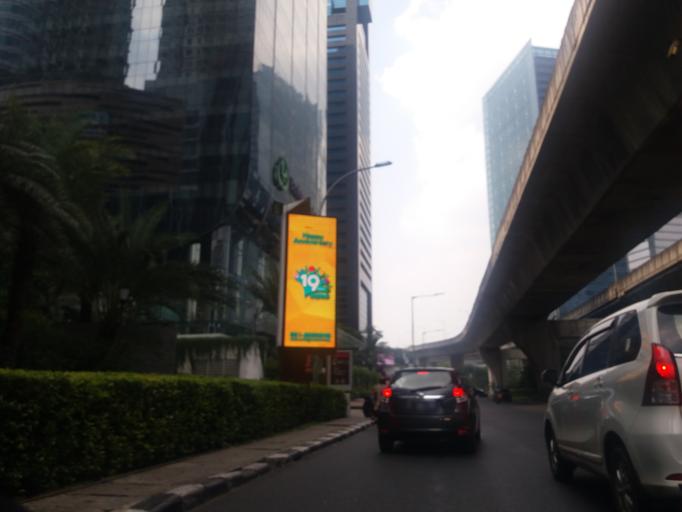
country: ID
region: Jakarta Raya
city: Jakarta
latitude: -6.2253
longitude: 106.8303
